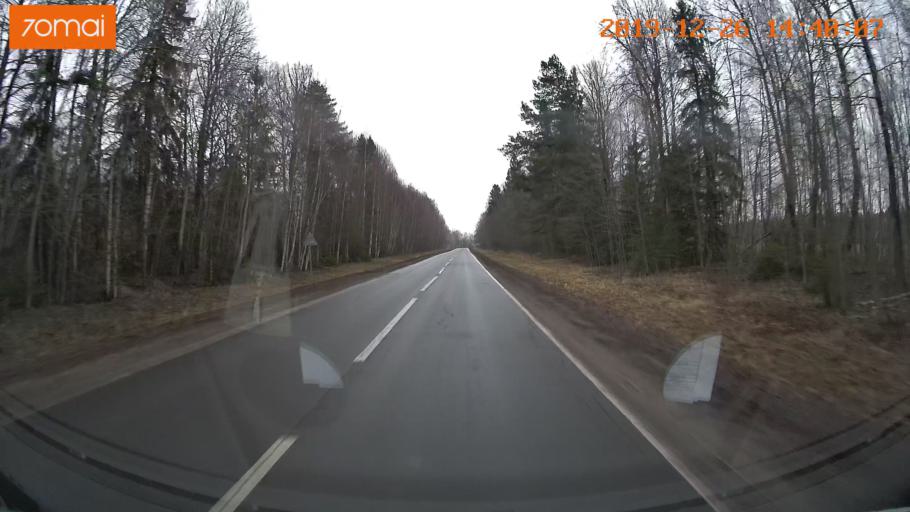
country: RU
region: Jaroslavl
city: Poshekhon'ye
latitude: 58.3779
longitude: 38.9920
